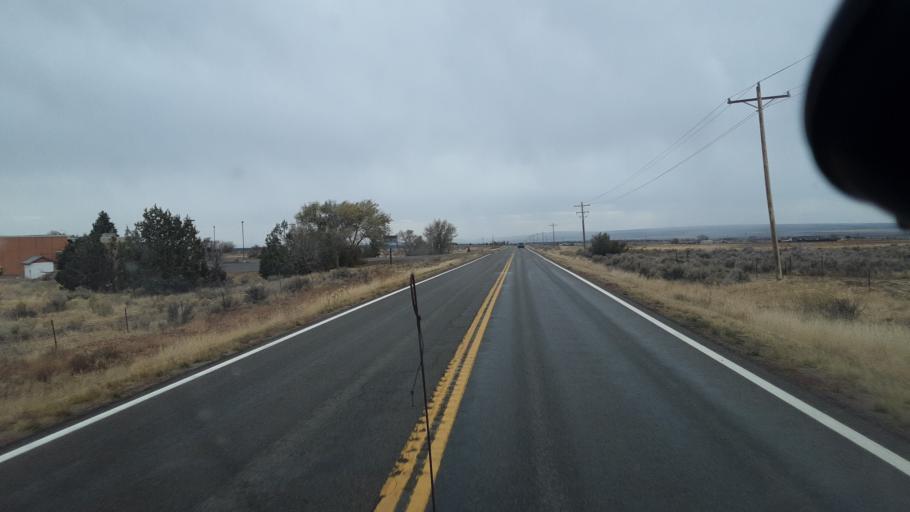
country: US
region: Colorado
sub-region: Montezuma County
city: Mancos
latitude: 37.1471
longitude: -108.1209
